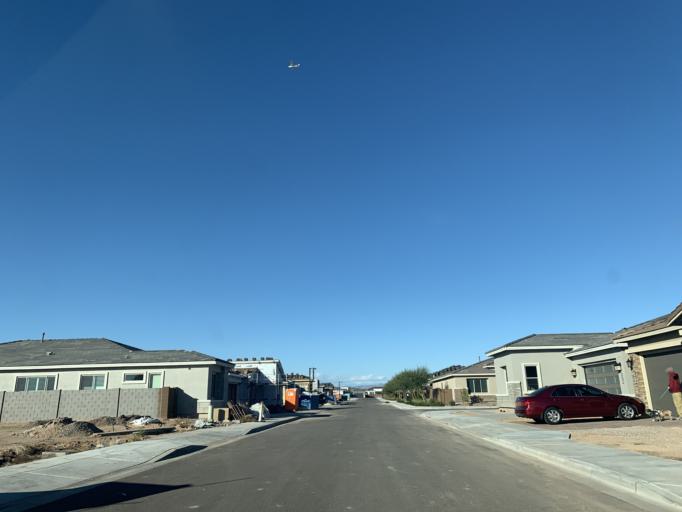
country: US
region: Arizona
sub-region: Maricopa County
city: Cave Creek
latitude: 33.6883
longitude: -112.0221
